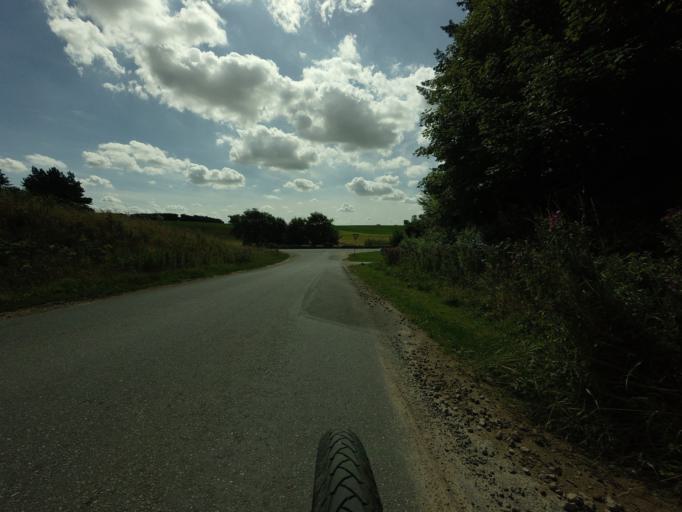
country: DK
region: North Denmark
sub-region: Hjorring Kommune
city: Hjorring
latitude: 57.4532
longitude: 9.9094
